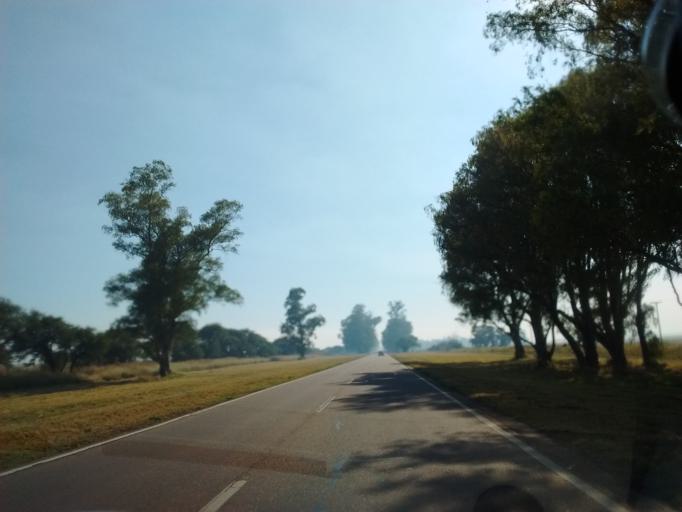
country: AR
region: La Pampa
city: Anguil
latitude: -36.5708
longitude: -64.1452
